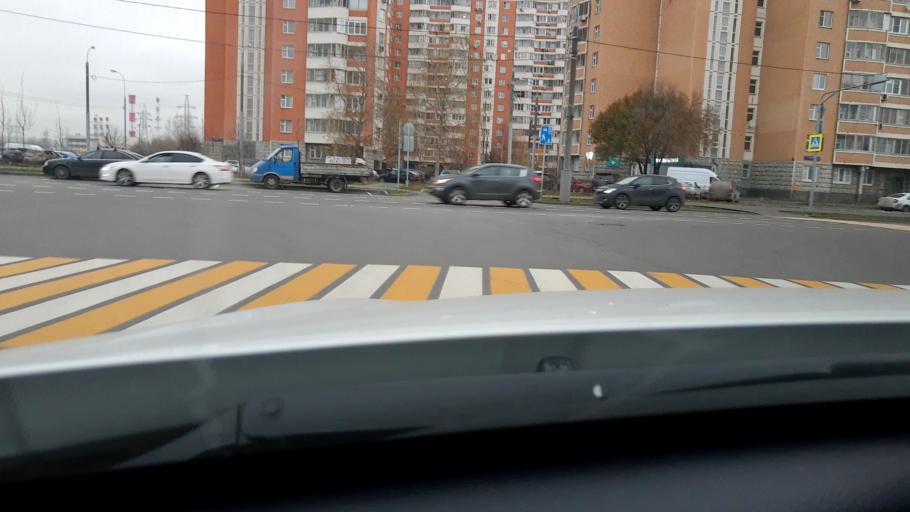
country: RU
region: Moscow
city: Zhulebino
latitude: 55.7145
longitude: 37.8793
